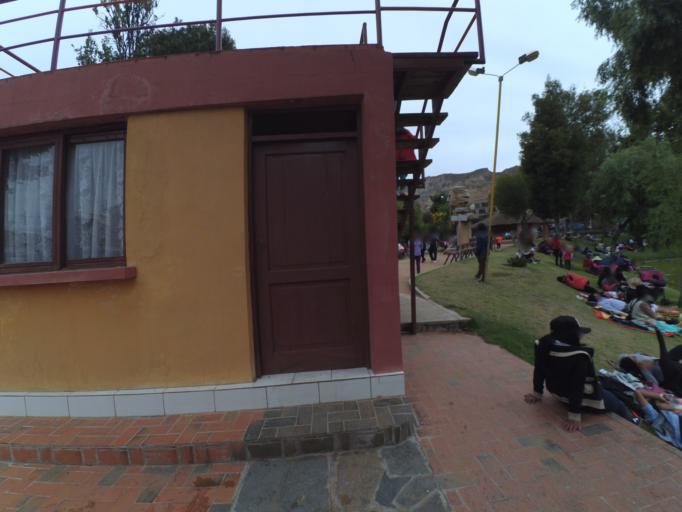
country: BO
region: La Paz
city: La Paz
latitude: -16.5416
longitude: -68.0647
